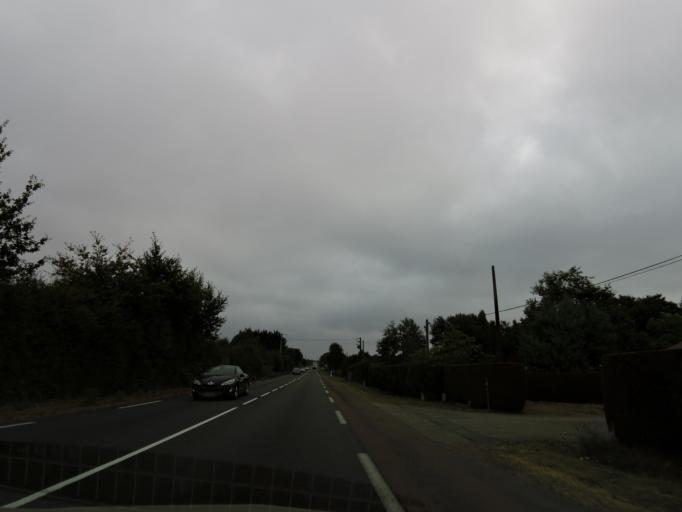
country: FR
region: Pays de la Loire
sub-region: Departement de la Vendee
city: La Boissiere-des-Landes
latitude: 46.5622
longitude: -1.4507
